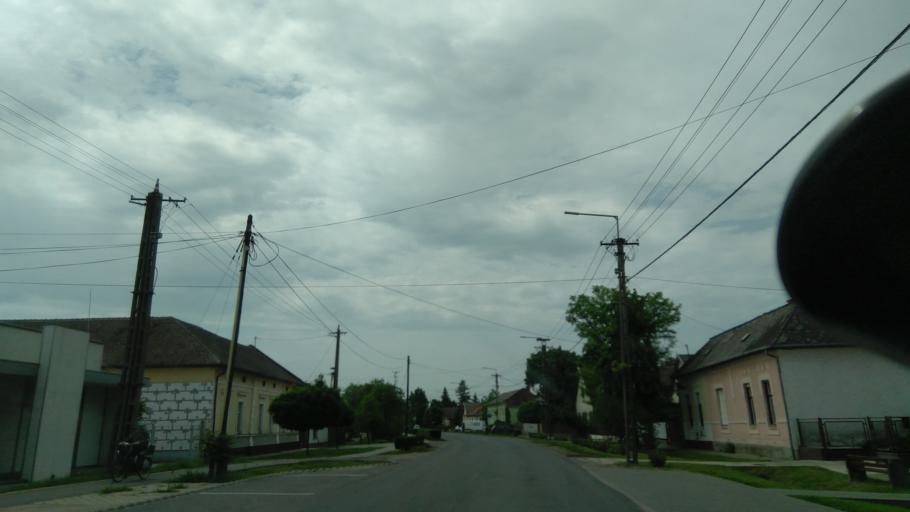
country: HU
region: Bekes
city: Fuzesgyarmat
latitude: 47.1066
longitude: 21.2111
